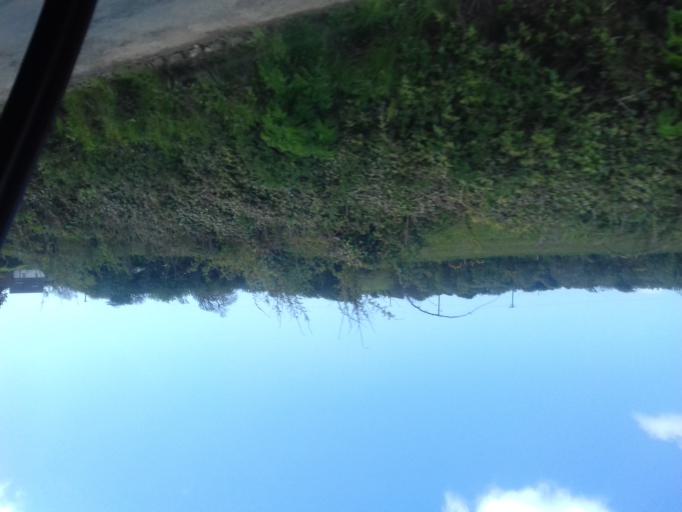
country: IE
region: Munster
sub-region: Waterford
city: Dunmore East
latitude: 52.1970
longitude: -6.8996
